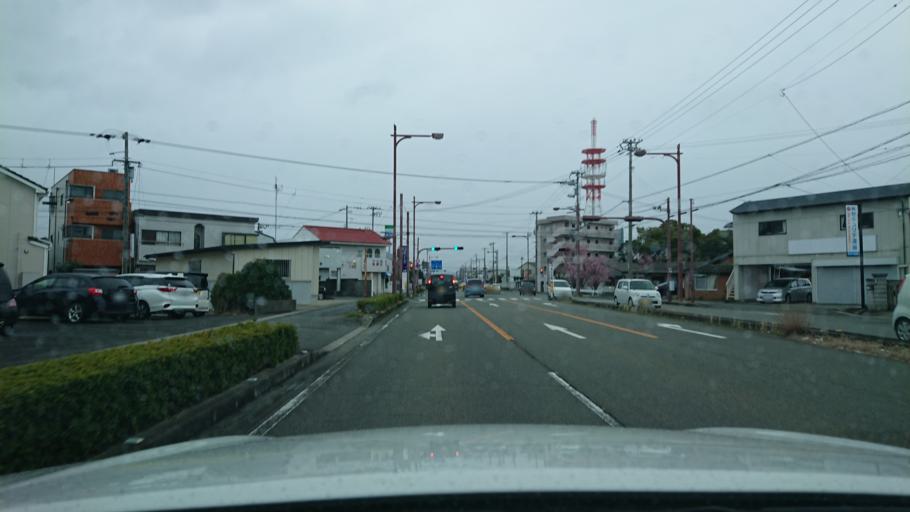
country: JP
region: Tokushima
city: Tokushima-shi
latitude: 34.0836
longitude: 134.5173
